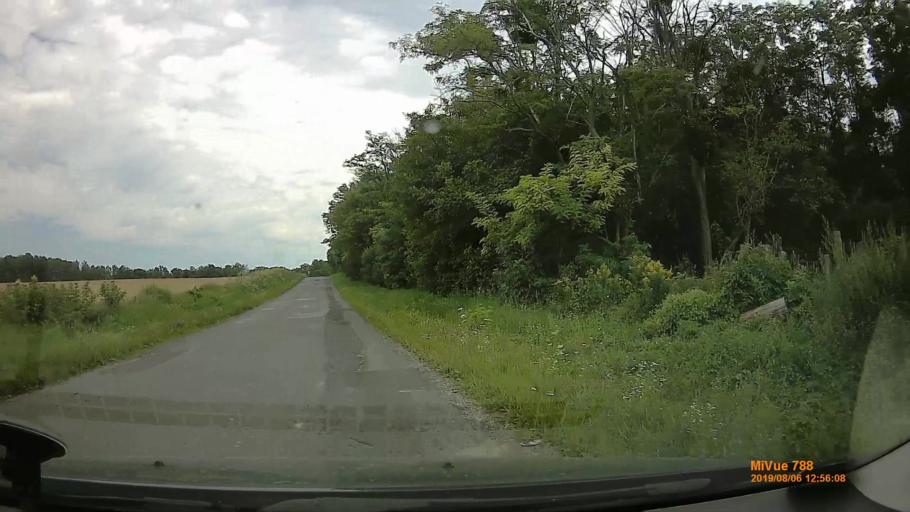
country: HU
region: Zala
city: Pacsa
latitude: 46.6349
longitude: 17.0266
